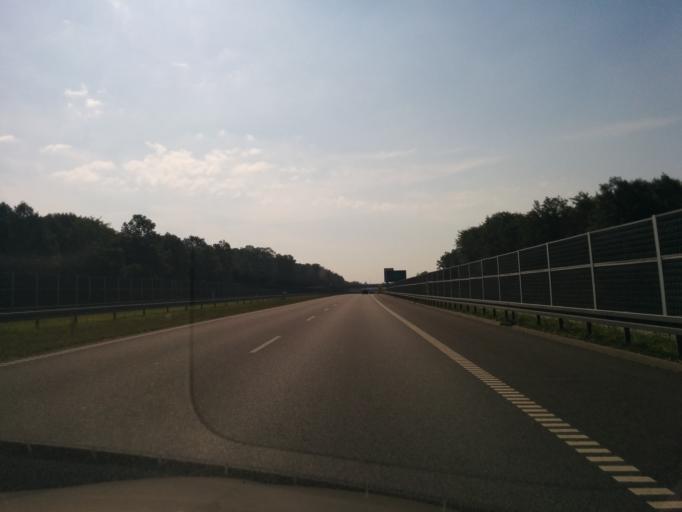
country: PL
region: Silesian Voivodeship
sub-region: Powiat tarnogorski
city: Radzionkow
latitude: 50.3796
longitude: 18.8688
